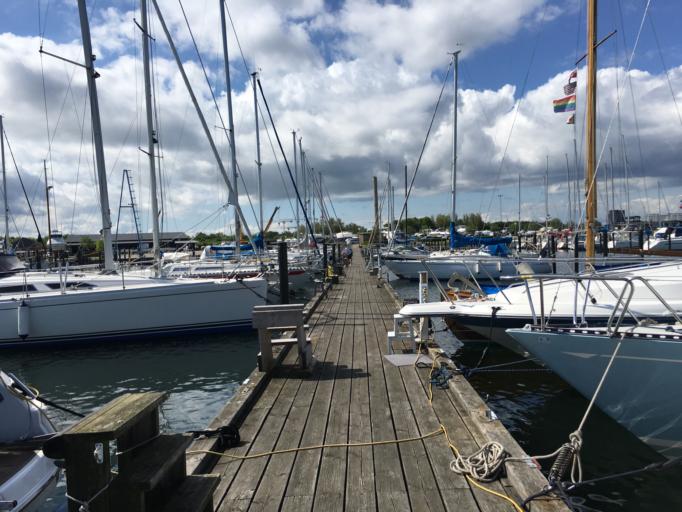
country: SE
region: Skane
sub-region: Malmo
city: Malmoe
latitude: 55.5975
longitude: 12.9369
